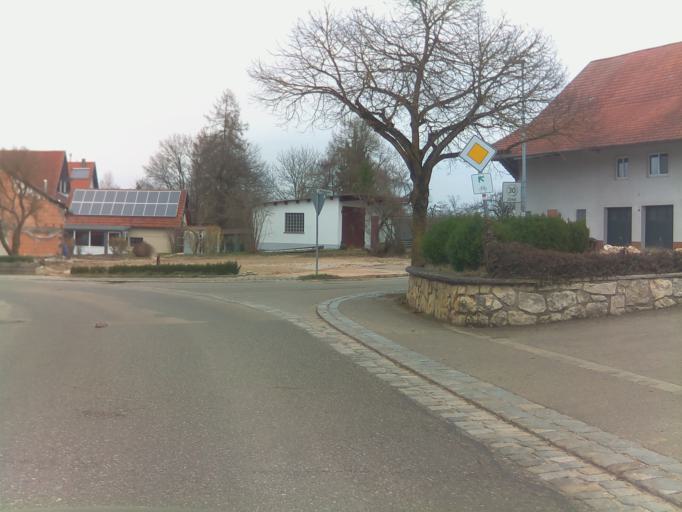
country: DE
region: Baden-Wuerttemberg
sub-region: Tuebingen Region
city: Schelklingen
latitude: 48.3871
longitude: 9.6656
